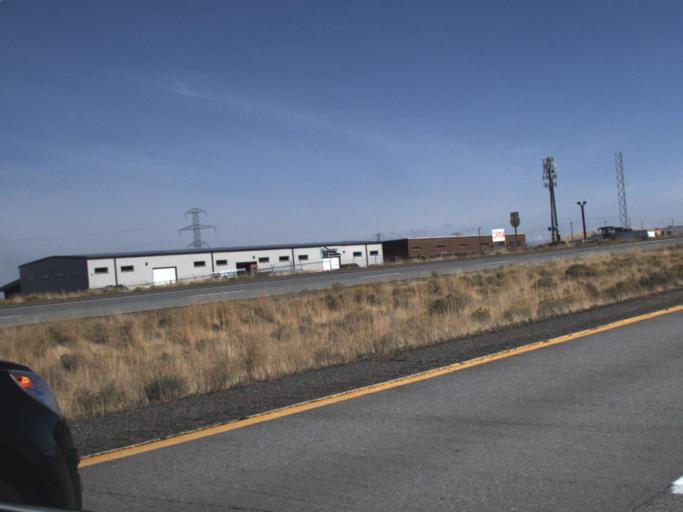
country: US
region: Washington
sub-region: Franklin County
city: West Pasco
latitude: 46.1718
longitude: -119.2090
